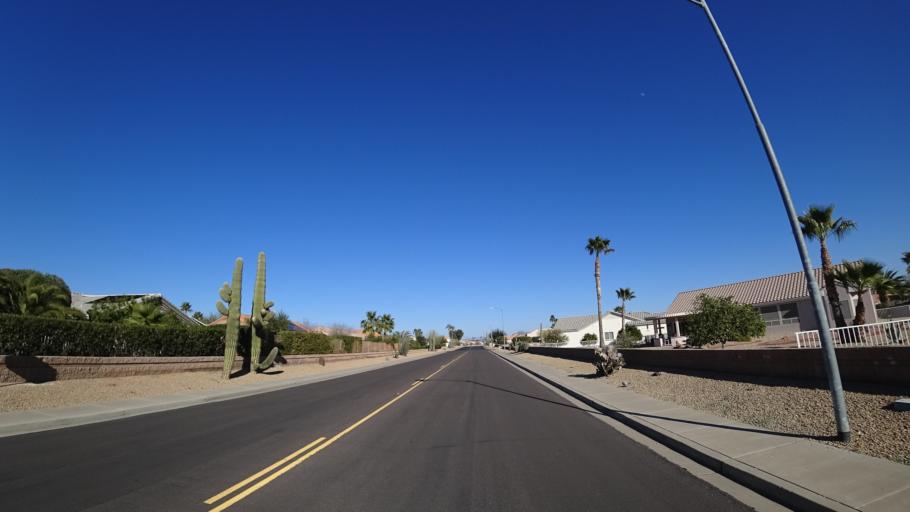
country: US
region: Arizona
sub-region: Maricopa County
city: Sun City West
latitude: 33.6922
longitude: -112.3790
